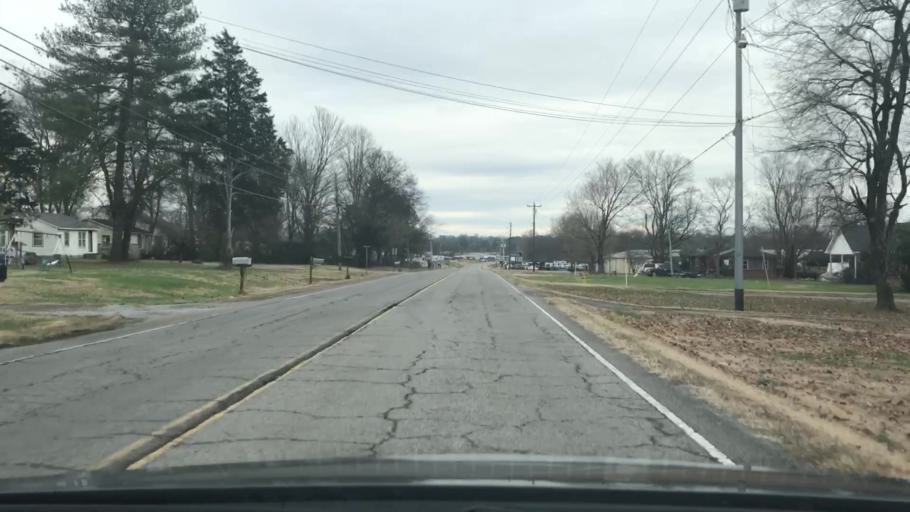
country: US
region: Tennessee
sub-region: Sumner County
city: Gallatin
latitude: 36.4190
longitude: -86.4566
